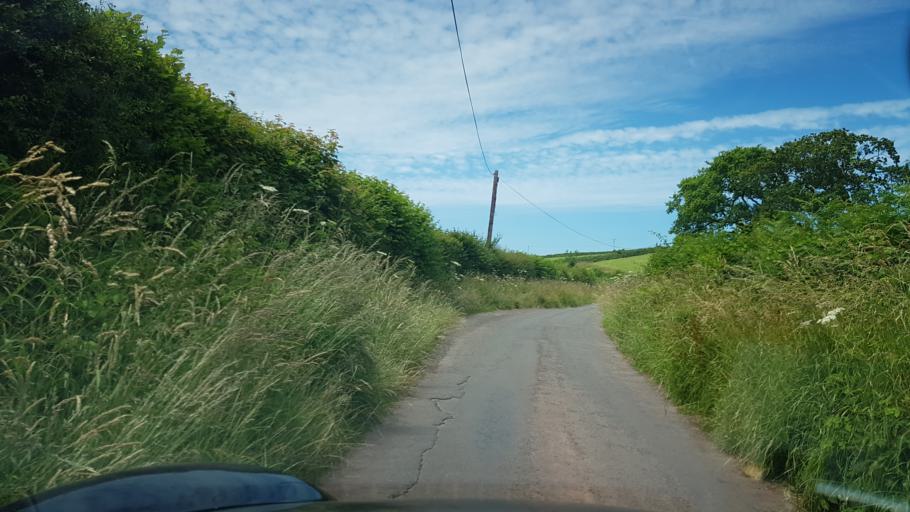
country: GB
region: Wales
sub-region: Carmarthenshire
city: Saint Clears
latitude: 51.7697
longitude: -4.4755
